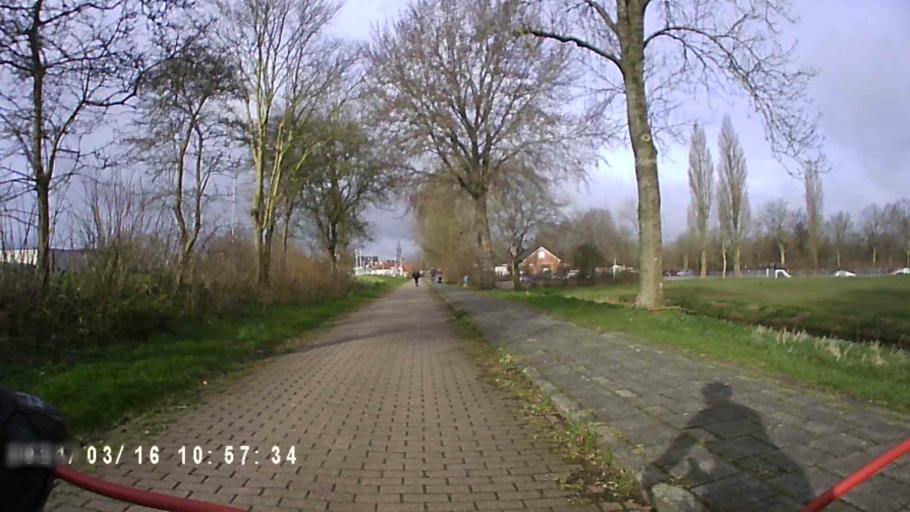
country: NL
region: Friesland
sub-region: Gemeente Dongeradeel
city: Dokkum
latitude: 53.3258
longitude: 6.0072
